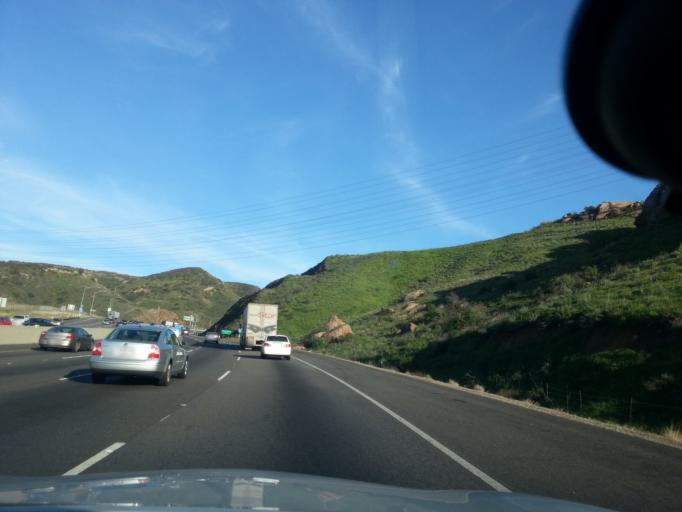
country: US
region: California
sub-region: Ventura County
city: Casa Conejo
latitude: 34.2001
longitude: -118.9629
